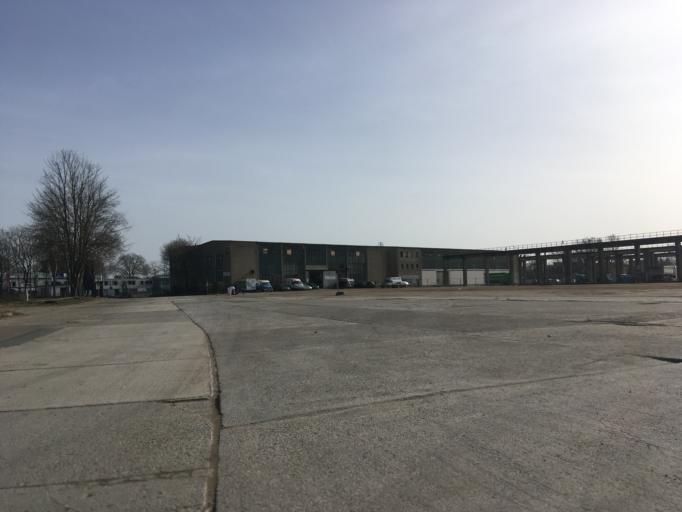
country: DE
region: Berlin
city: Kopenick Bezirk
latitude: 52.4303
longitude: 13.5692
